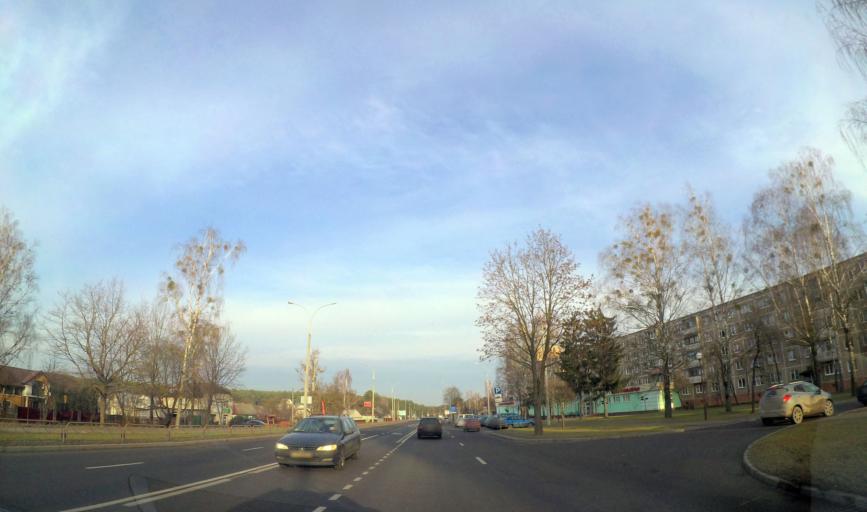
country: BY
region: Grodnenskaya
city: Hrodna
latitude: 53.6705
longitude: 23.7917
